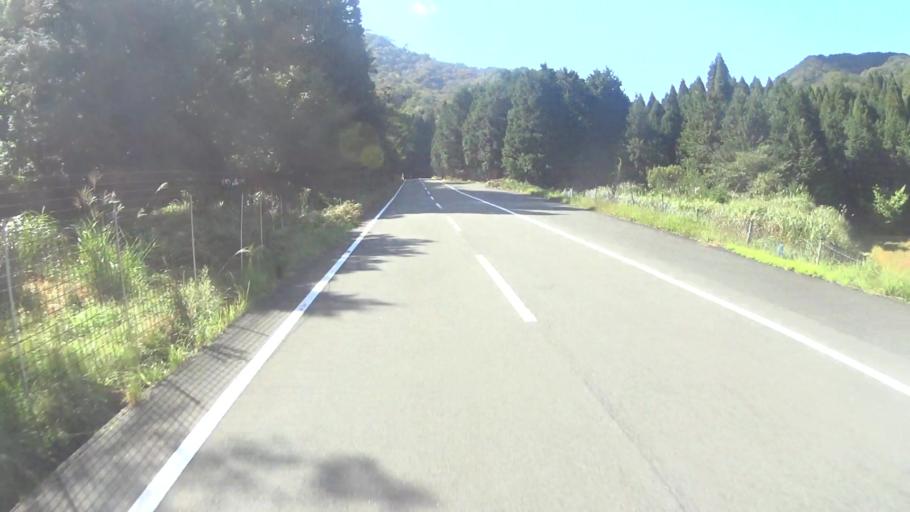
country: JP
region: Hyogo
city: Toyooka
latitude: 35.5350
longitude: 134.9300
